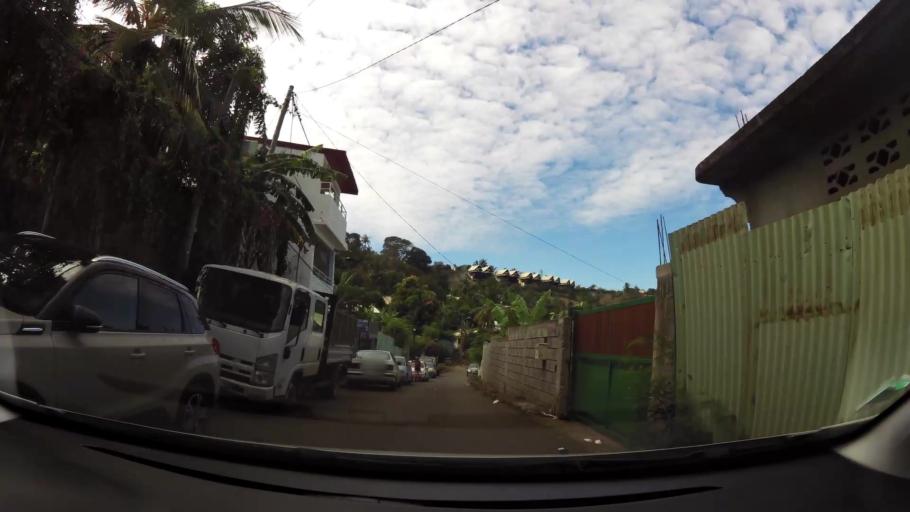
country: YT
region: Mamoudzou
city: Mamoudzou
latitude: -12.7804
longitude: 45.2202
